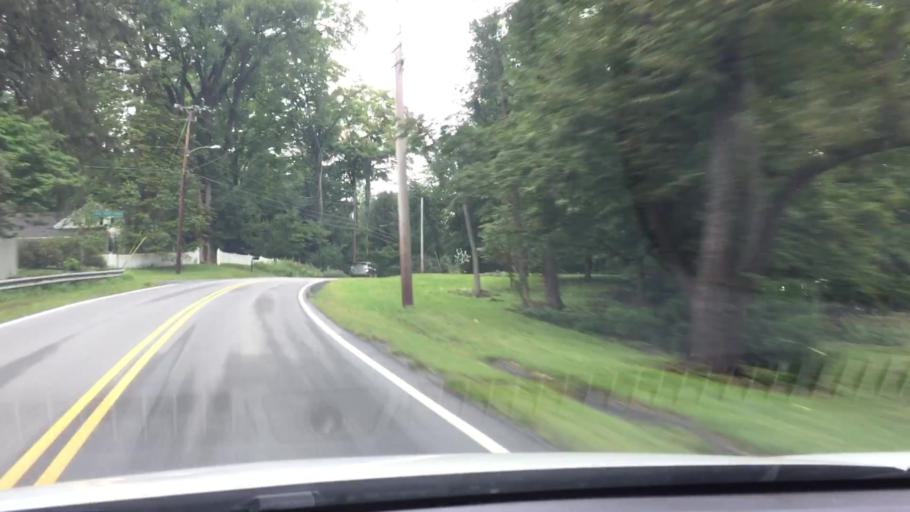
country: US
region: Massachusetts
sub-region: Berkshire County
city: Housatonic
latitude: 42.2642
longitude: -73.3805
